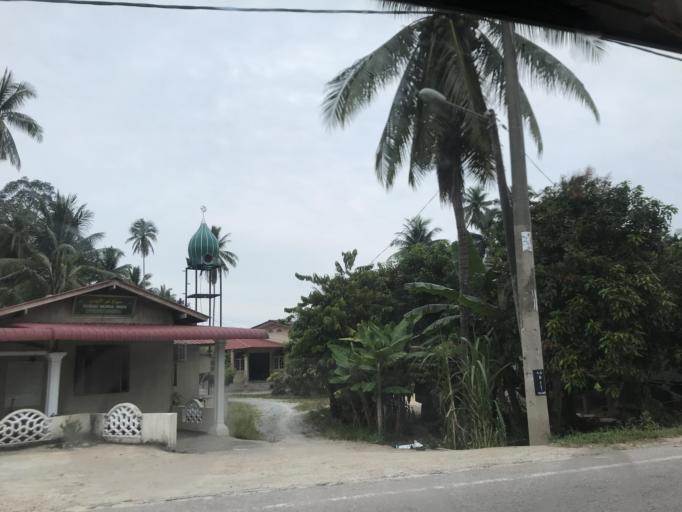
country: MY
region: Kelantan
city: Kota Bharu
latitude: 6.1717
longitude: 102.2297
